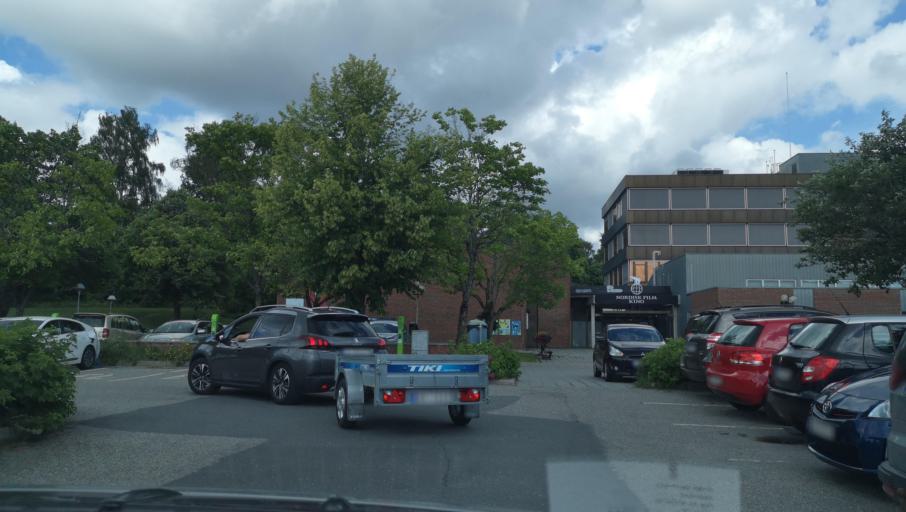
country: NO
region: Ostfold
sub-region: Askim
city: Askim
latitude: 59.5841
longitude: 11.1600
